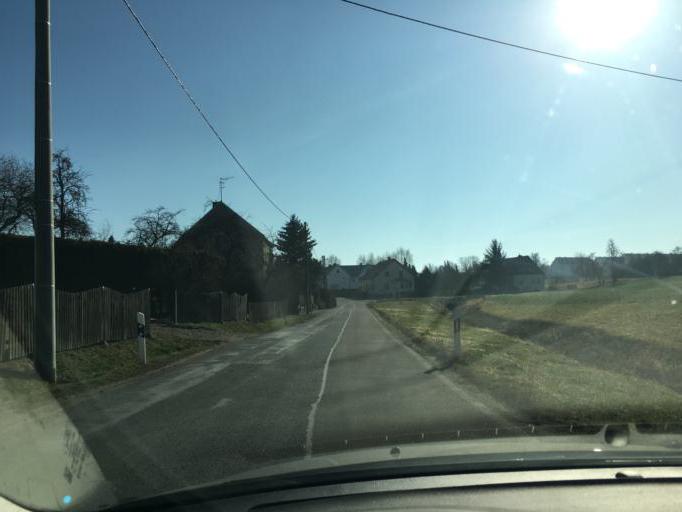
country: DE
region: Saxony
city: Narsdorf
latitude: 51.0178
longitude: 12.7126
